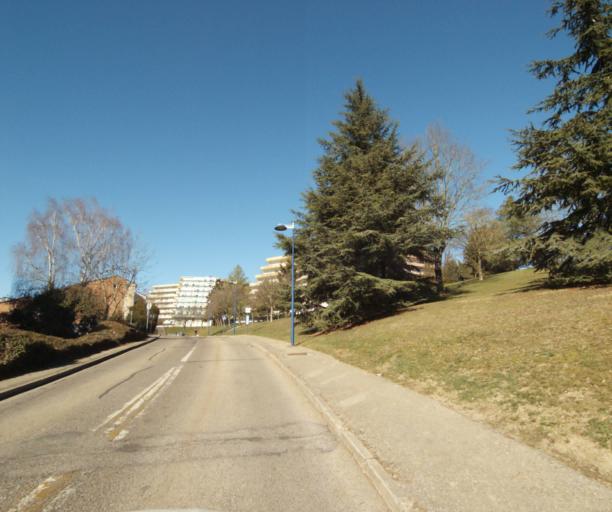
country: FR
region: Lorraine
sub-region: Departement de Meurthe-et-Moselle
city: Ludres
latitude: 48.6144
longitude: 6.1674
